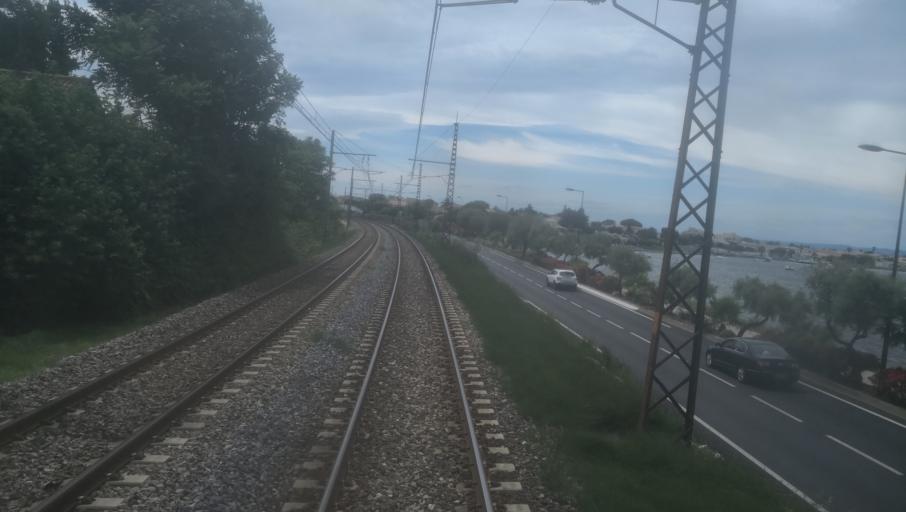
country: FR
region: Languedoc-Roussillon
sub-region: Departement de l'Herault
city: Sete
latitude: 43.4142
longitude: 3.6750
